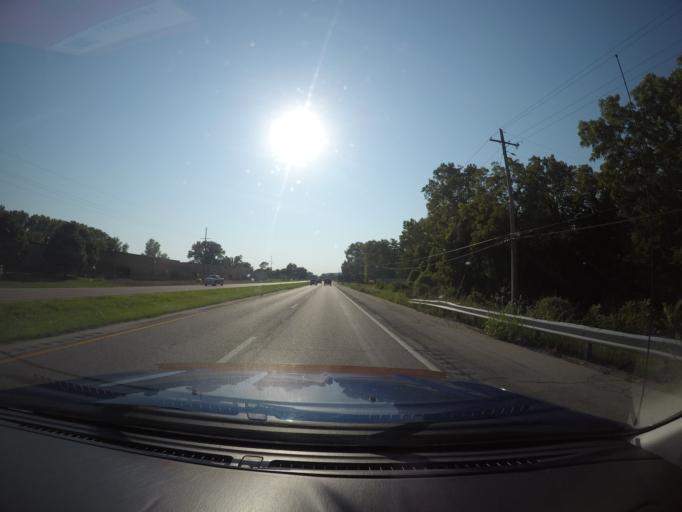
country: US
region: Kansas
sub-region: Wyandotte County
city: Edwardsville
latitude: 39.0637
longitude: -94.8343
